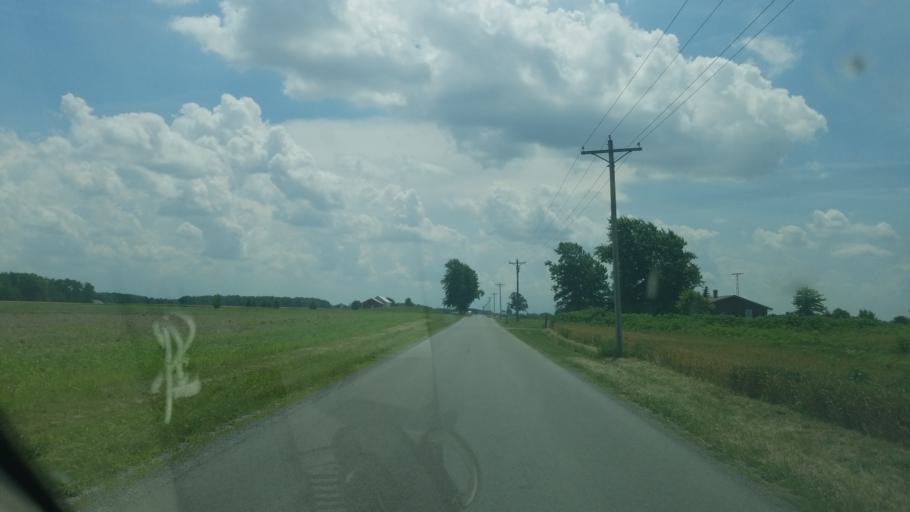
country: US
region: Ohio
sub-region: Hancock County
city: Arlington
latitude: 40.8427
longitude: -83.5998
